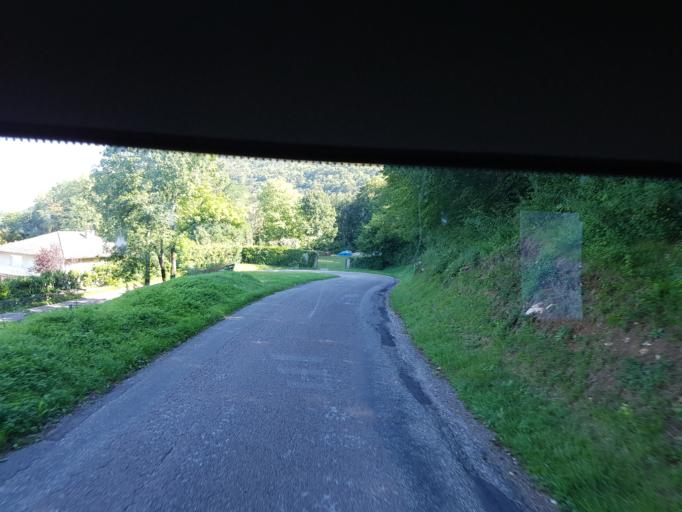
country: FR
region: Franche-Comte
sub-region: Departement du Jura
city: Perrigny
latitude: 46.6979
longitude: 5.6008
